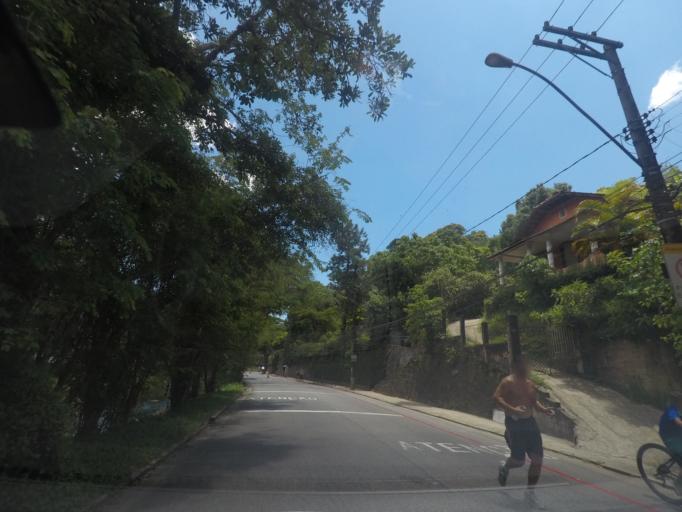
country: BR
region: Rio de Janeiro
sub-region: Petropolis
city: Petropolis
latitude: -22.5000
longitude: -43.1807
